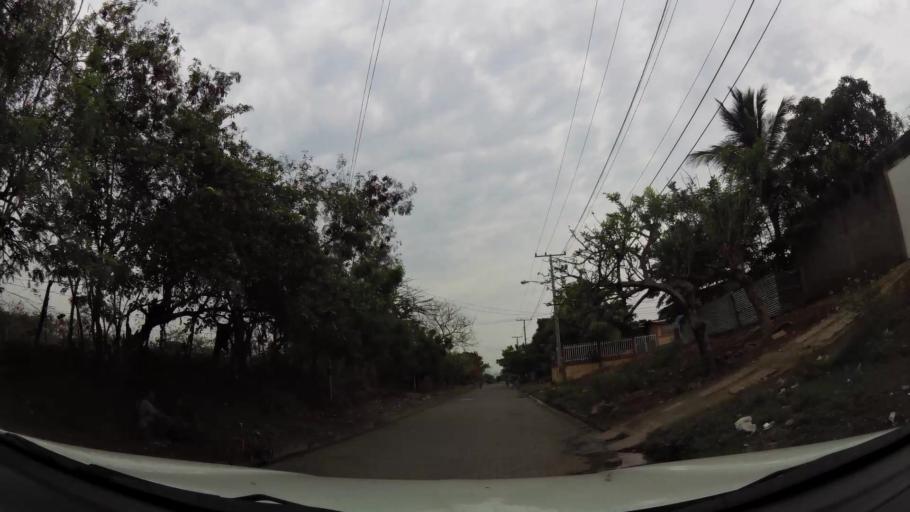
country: NI
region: Granada
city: Granada
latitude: 11.9356
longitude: -85.9474
